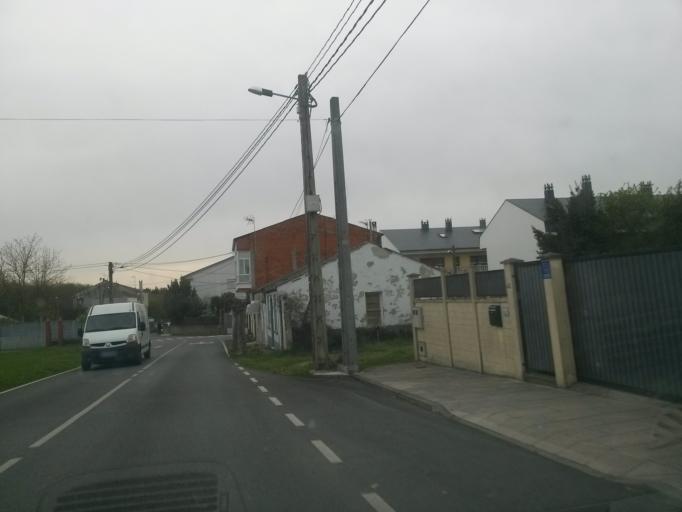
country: ES
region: Galicia
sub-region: Provincia de Lugo
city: Lugo
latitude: 43.0268
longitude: -7.5523
